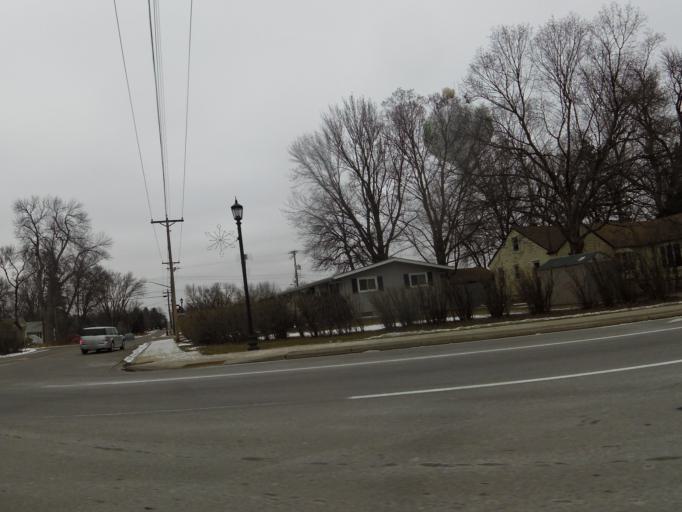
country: US
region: Minnesota
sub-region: Hennepin County
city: Maple Plain
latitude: 45.0081
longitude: -93.6558
